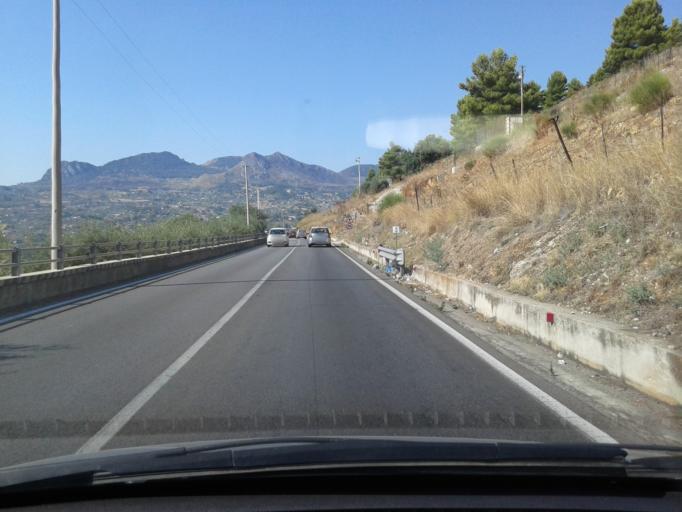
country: IT
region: Sicily
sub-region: Palermo
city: Cannizzaro-Favara
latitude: 38.0628
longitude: 13.2647
